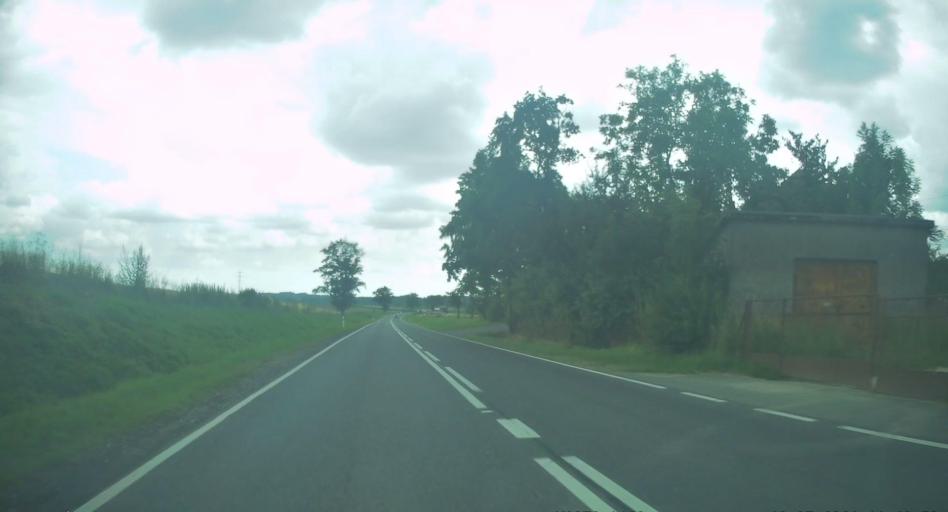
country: PL
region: Opole Voivodeship
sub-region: Powiat prudnicki
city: Laka Prudnicka
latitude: 50.4127
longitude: 17.4960
